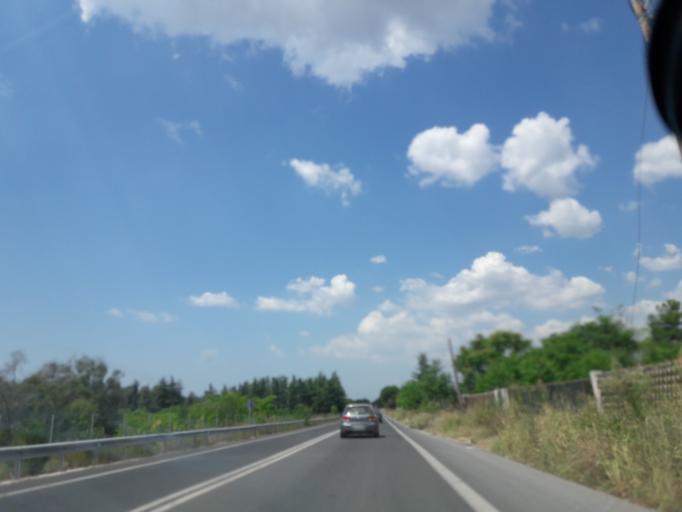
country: GR
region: Central Macedonia
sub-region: Nomos Thessalonikis
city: Souroti
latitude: 40.5075
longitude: 23.0876
